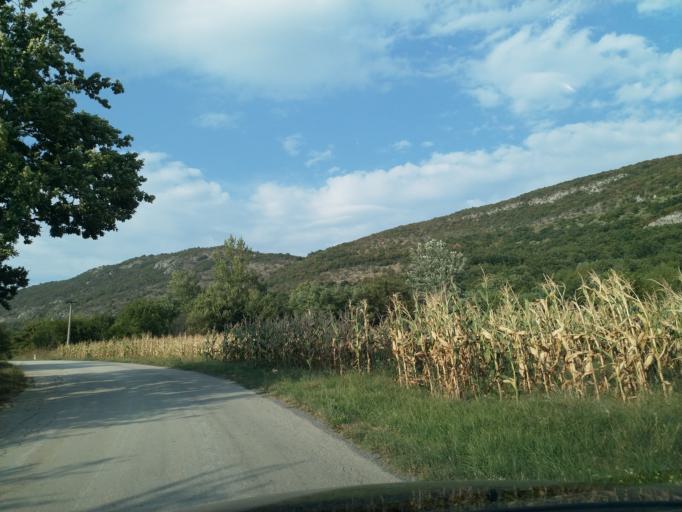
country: RS
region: Central Serbia
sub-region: Pomoravski Okrug
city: Paracin
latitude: 43.8348
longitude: 21.5406
